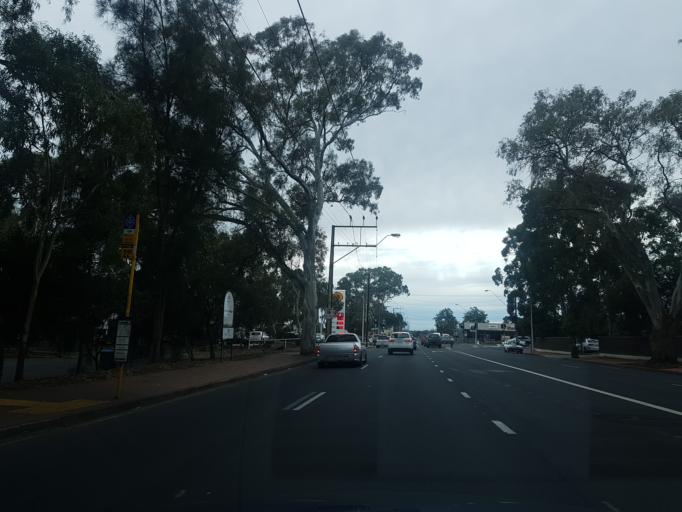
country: AU
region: South Australia
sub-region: Campbelltown
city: Campbelltown
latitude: -34.8897
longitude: 138.6743
